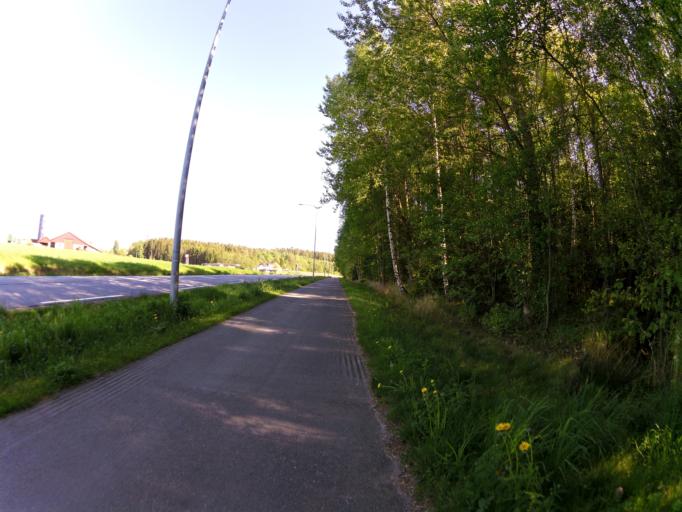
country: NO
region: Ostfold
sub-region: Sarpsborg
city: Sarpsborg
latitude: 59.2262
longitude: 11.0374
